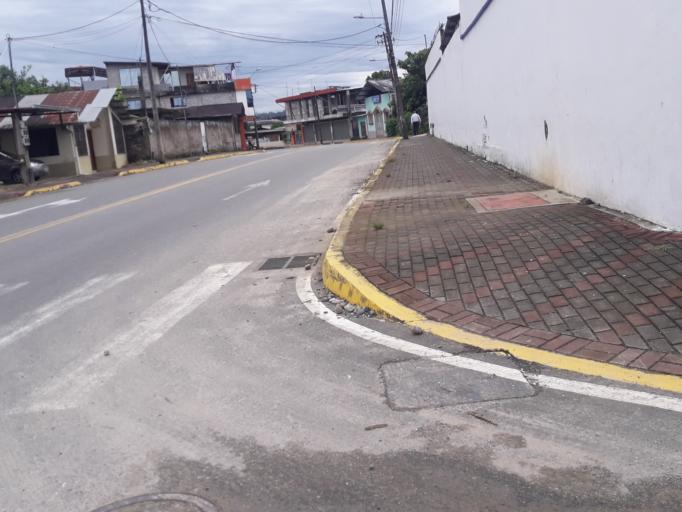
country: EC
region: Napo
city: Tena
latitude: -1.0033
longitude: -77.8146
